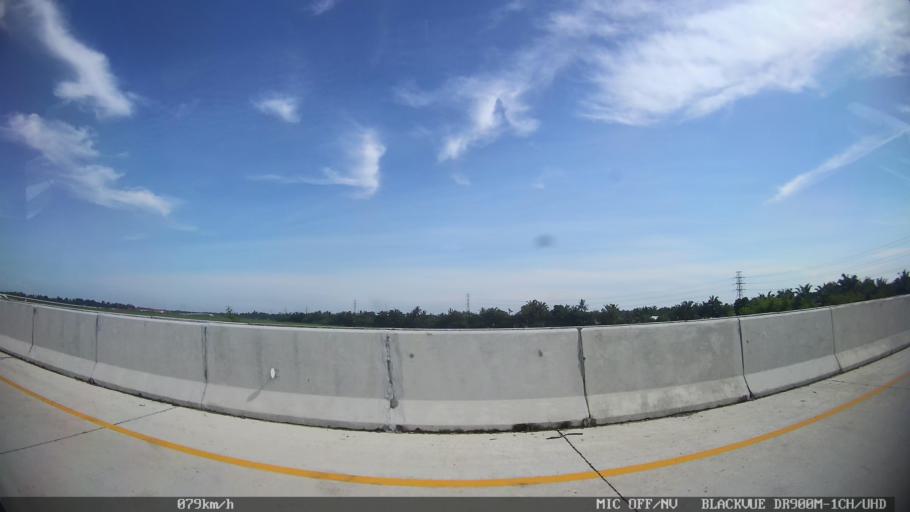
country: ID
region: North Sumatra
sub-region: Kabupaten Langkat
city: Stabat
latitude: 3.7135
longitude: 98.5017
